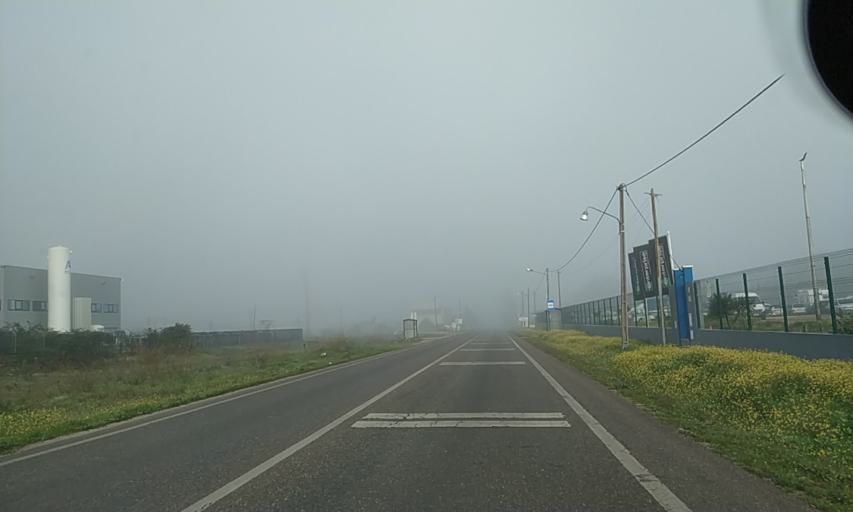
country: PT
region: Setubal
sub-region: Palmela
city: Pinhal Novo
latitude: 38.6112
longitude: -8.9101
